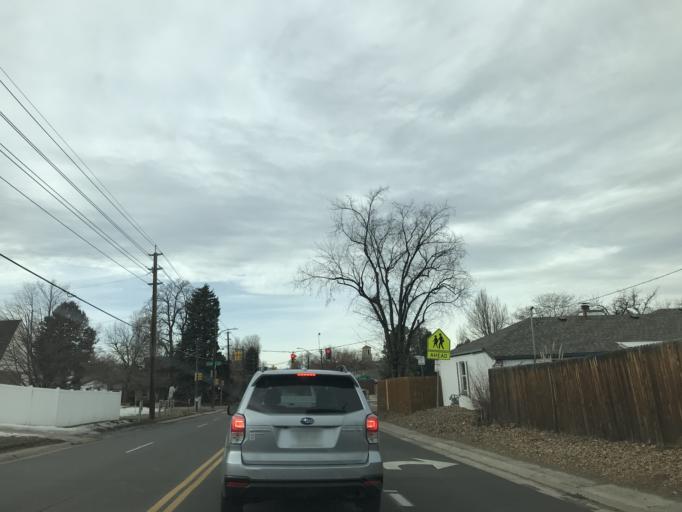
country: US
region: Colorado
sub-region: Arapahoe County
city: Glendale
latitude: 39.7293
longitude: -104.9240
